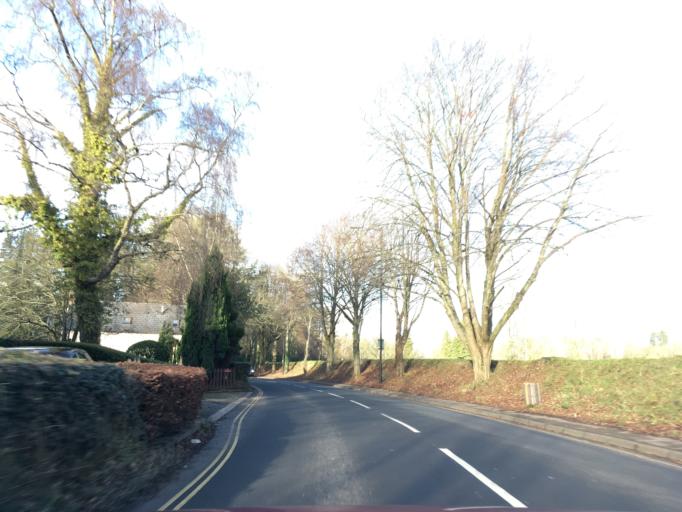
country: GB
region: Wales
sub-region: Monmouthshire
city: Usk
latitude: 51.7027
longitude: -2.9081
